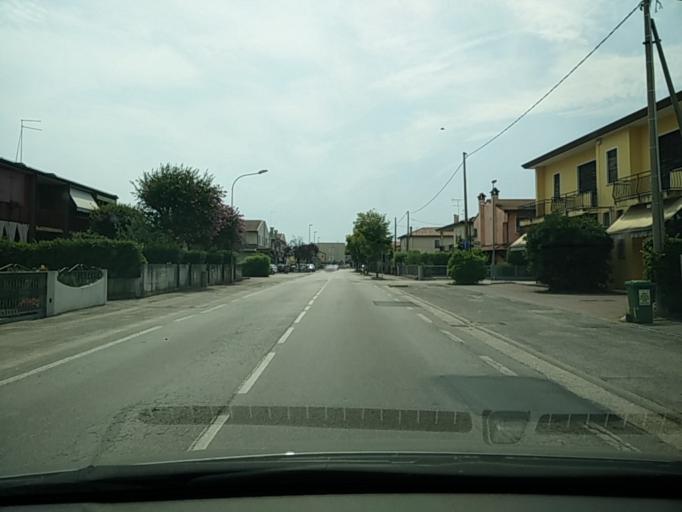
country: IT
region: Veneto
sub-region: Provincia di Treviso
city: San Floriano-Olmi
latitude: 45.6751
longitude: 12.3315
